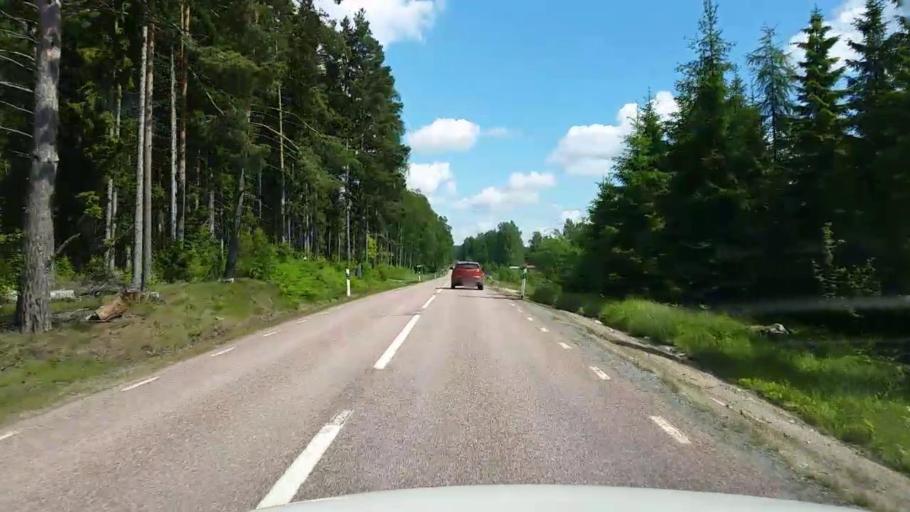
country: SE
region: Vaestmanland
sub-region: Skinnskattebergs Kommun
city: Skinnskatteberg
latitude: 59.7542
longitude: 15.8156
